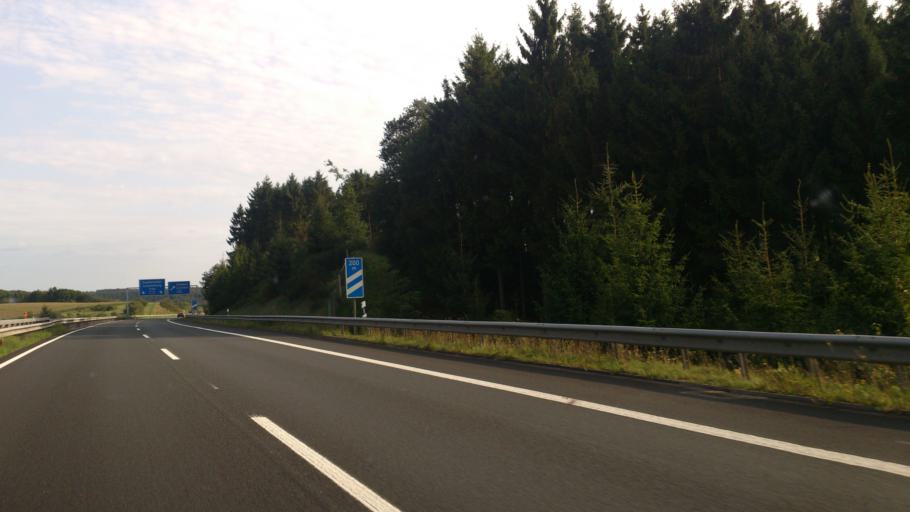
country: DE
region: Rheinland-Pfalz
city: Mehren
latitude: 50.1984
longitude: 6.8932
